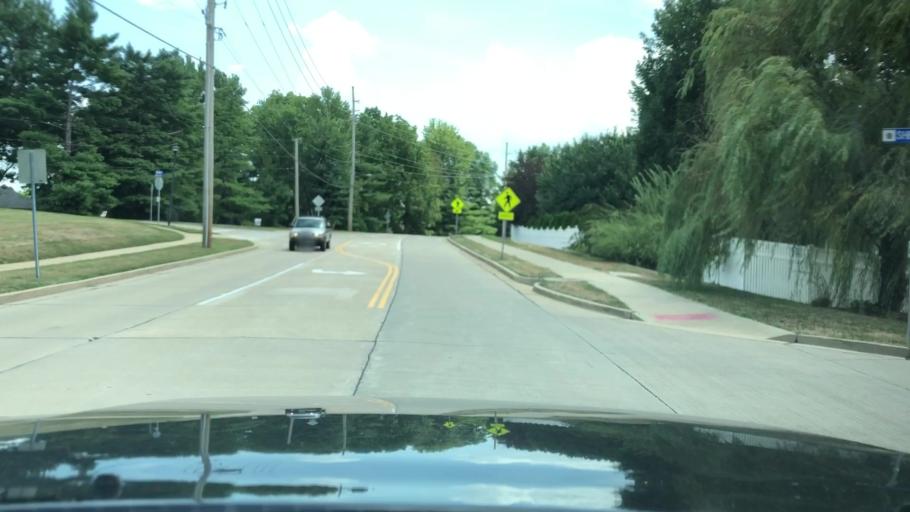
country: US
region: Missouri
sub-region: Saint Charles County
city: Saint Charles
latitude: 38.8068
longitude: -90.5361
